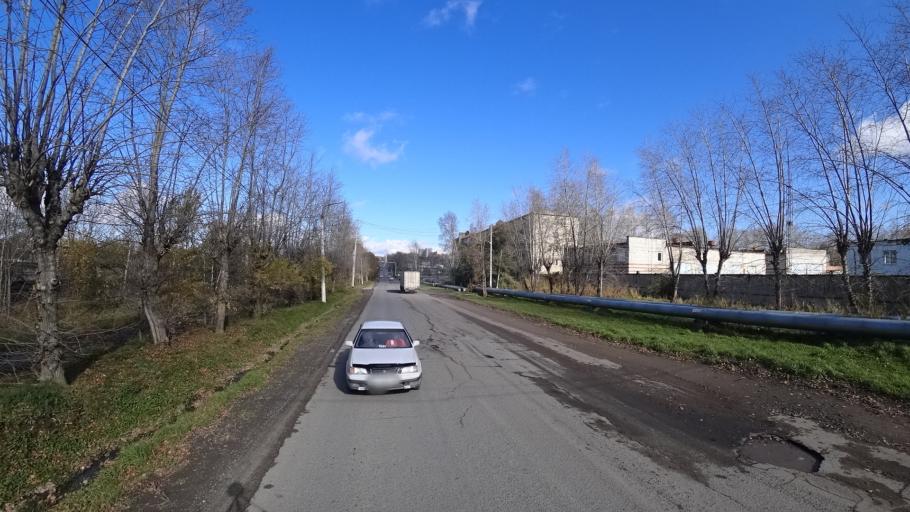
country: RU
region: Khabarovsk Krai
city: Amursk
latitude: 50.2245
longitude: 136.9015
